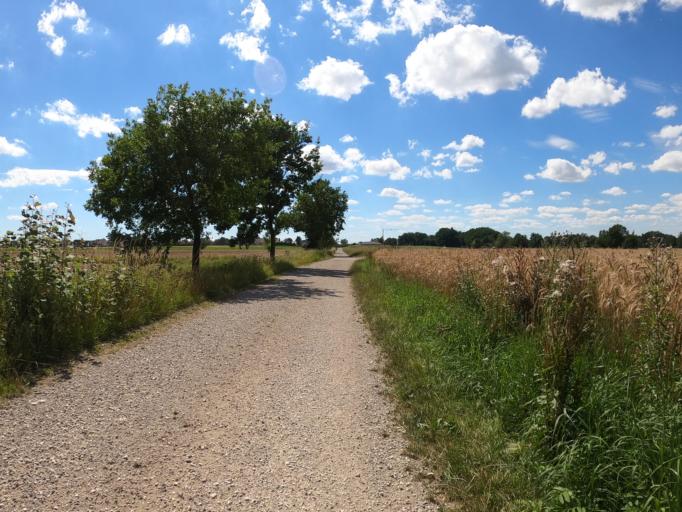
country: DE
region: Bavaria
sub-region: Swabia
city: Leipheim
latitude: 48.4221
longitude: 10.1999
